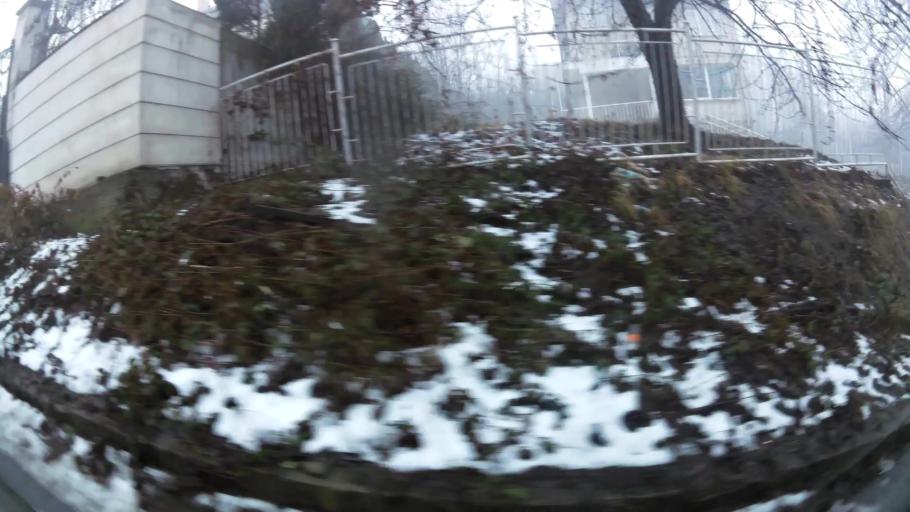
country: BG
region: Sofia-Capital
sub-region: Stolichna Obshtina
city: Sofia
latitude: 42.6615
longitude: 23.2594
